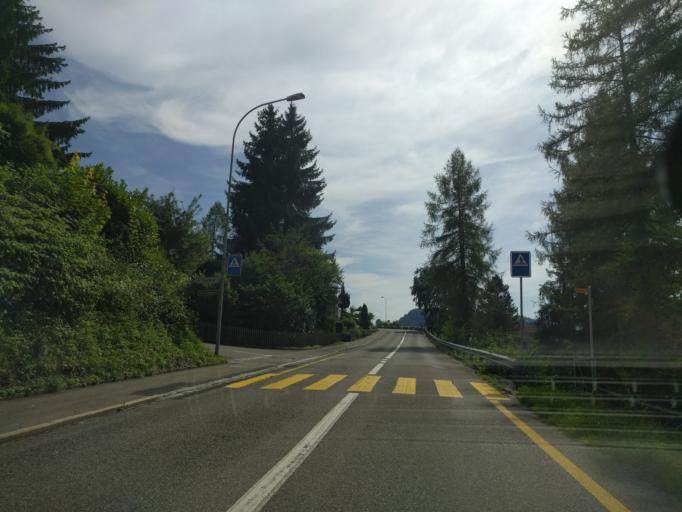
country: CH
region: Saint Gallen
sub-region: Wahlkreis Toggenburg
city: Lichtensteig
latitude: 47.3242
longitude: 9.0913
